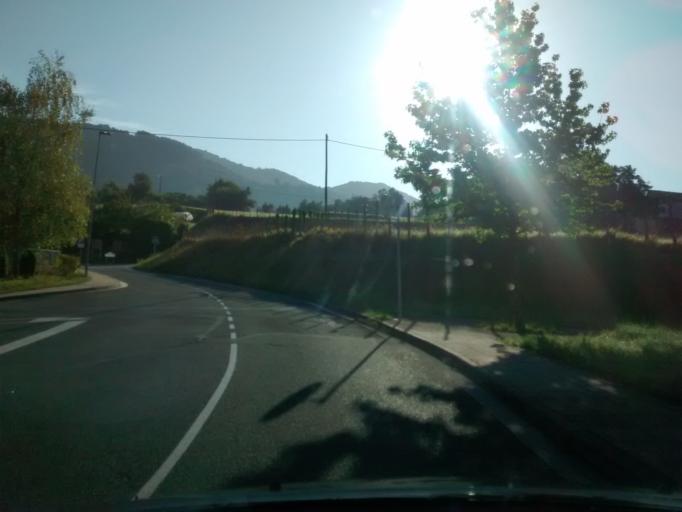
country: ES
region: Basque Country
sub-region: Provincia de Guipuzcoa
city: Mendaro
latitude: 43.2493
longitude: -2.3890
